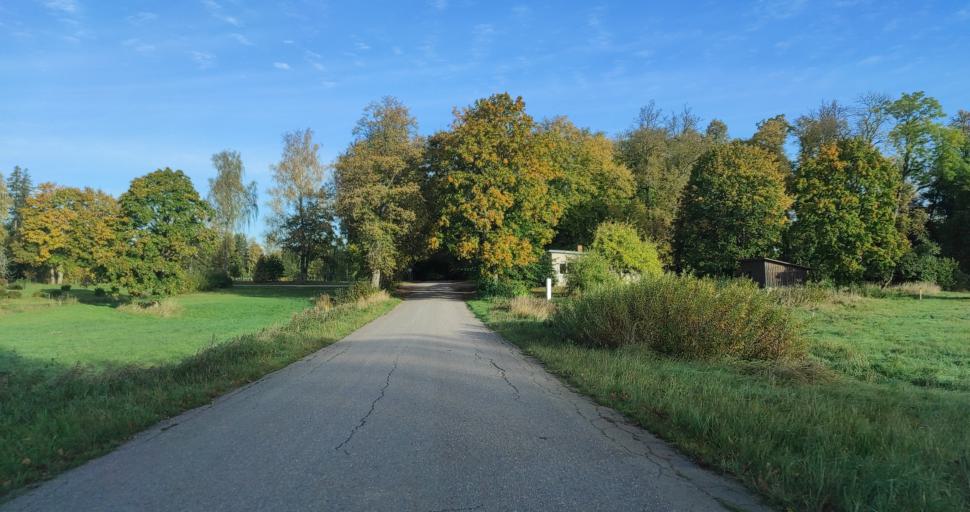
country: LV
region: Skrunda
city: Skrunda
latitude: 56.7442
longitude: 21.8785
